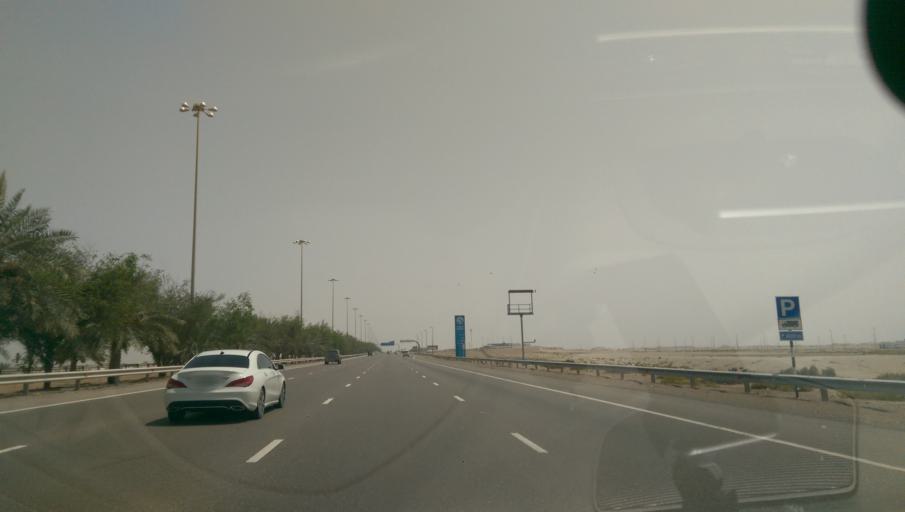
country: AE
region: Abu Dhabi
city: Abu Dhabi
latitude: 24.3805
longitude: 54.6598
